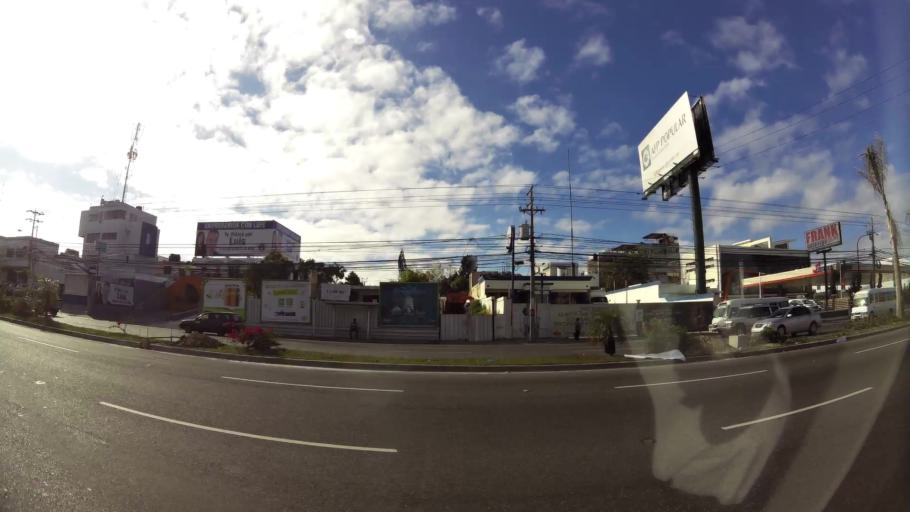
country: DO
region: Nacional
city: Bella Vista
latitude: 18.4587
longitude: -69.9441
